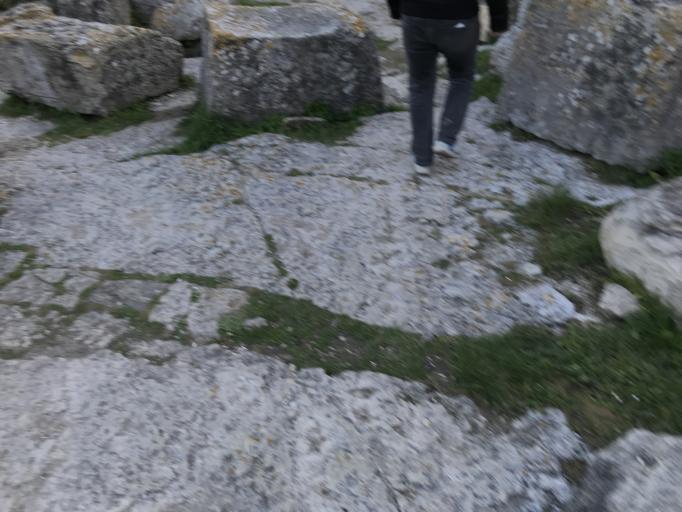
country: TR
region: Hatay
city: Buyukcat
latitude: 36.0915
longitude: 36.0356
